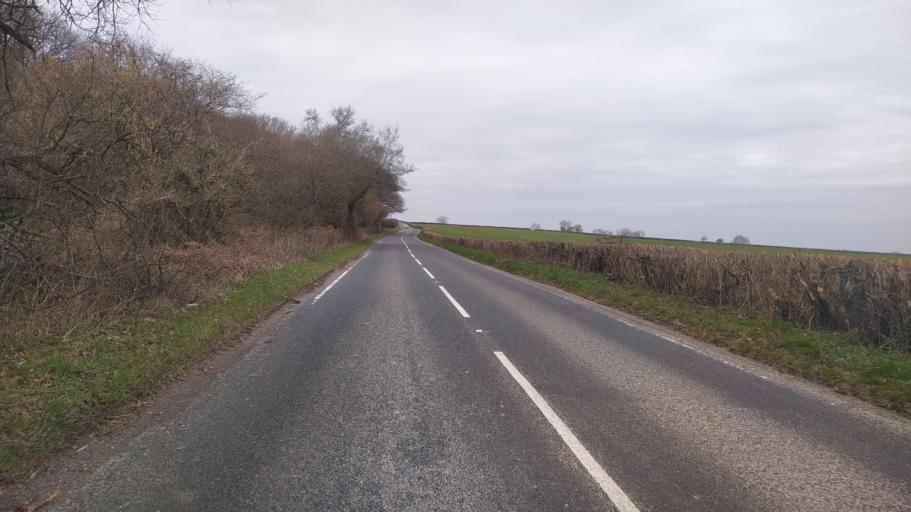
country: GB
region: England
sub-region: Dorset
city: Beaminster
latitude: 50.8216
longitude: -2.6661
